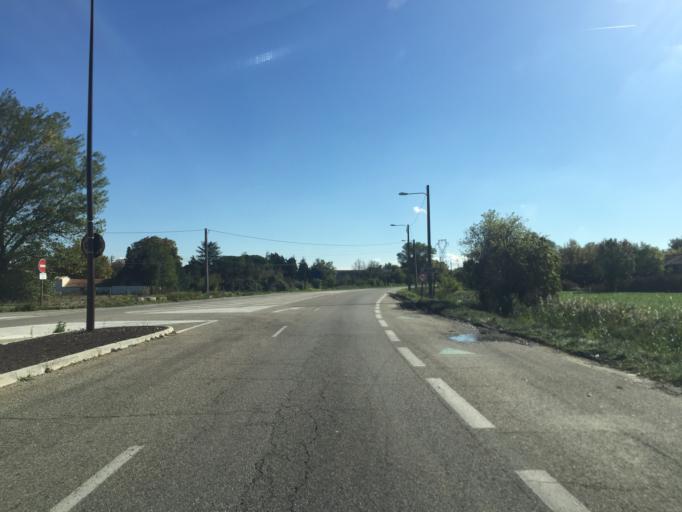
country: FR
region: Provence-Alpes-Cote d'Azur
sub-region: Departement du Vaucluse
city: Montfavet
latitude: 43.9348
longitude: 4.8539
